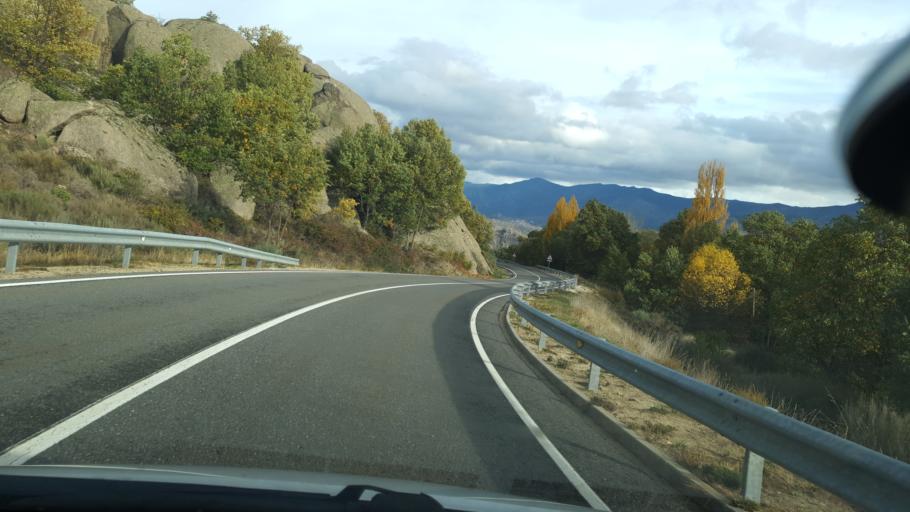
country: ES
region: Castille and Leon
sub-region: Provincia de Avila
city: Navalosa
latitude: 40.3943
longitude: -4.9120
